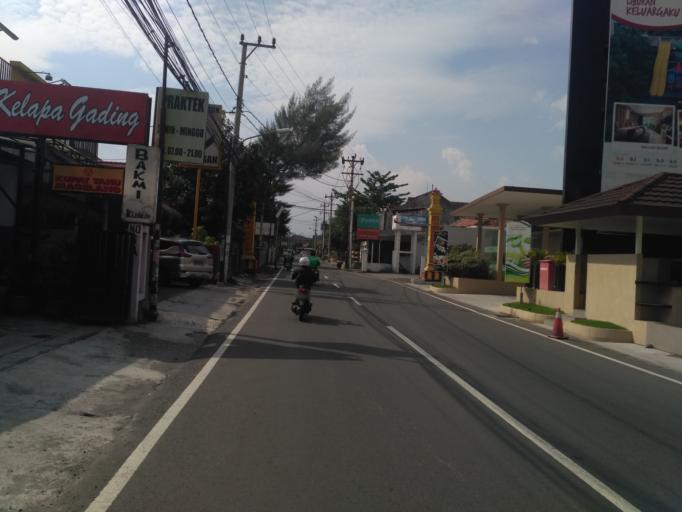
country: ID
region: Daerah Istimewa Yogyakarta
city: Depok
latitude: -7.7813
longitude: 110.4084
